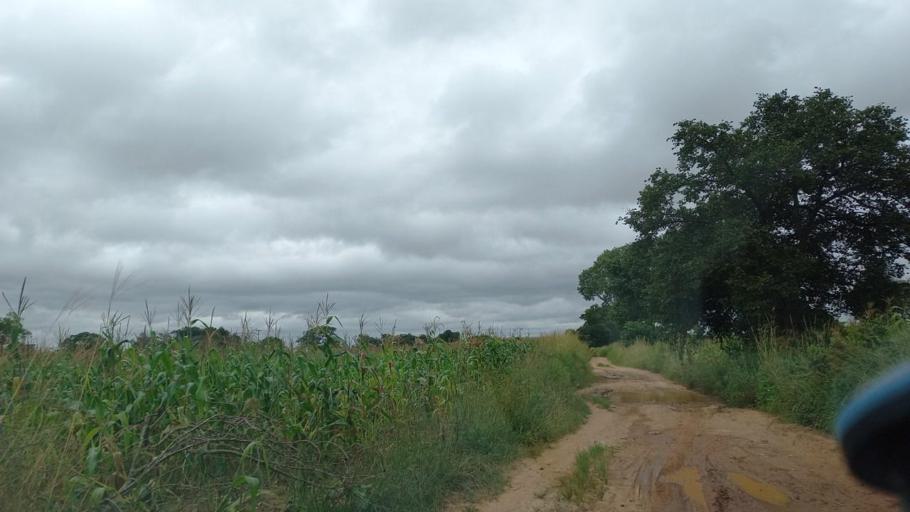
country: ZM
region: Lusaka
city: Lusaka
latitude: -15.1179
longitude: 28.3728
